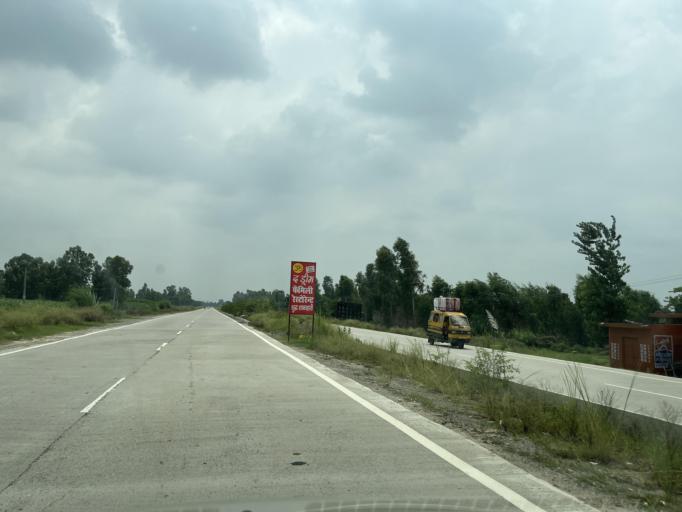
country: IN
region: Uttar Pradesh
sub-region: Bijnor
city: Najibabad
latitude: 29.5602
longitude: 78.3390
